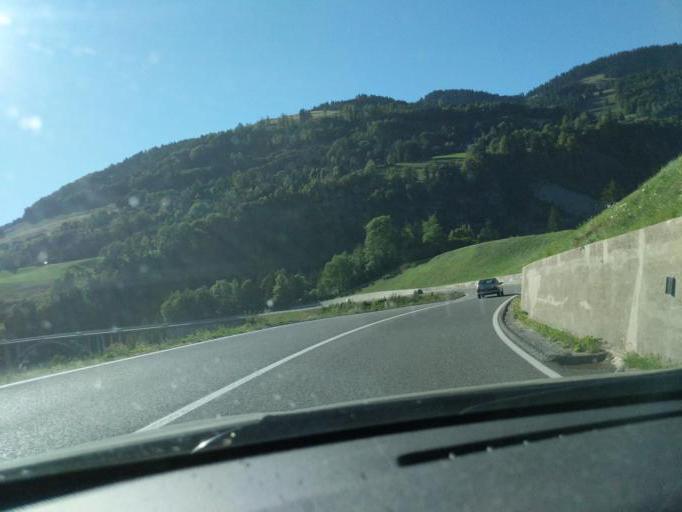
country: CH
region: Fribourg
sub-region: Gruyere District
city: Charmey
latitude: 46.6213
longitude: 7.1548
